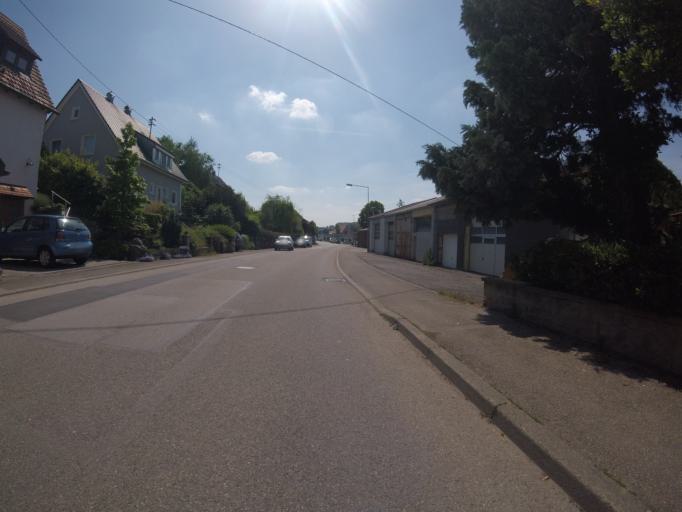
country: DE
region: Baden-Wuerttemberg
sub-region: Regierungsbezirk Stuttgart
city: Grossbottwar
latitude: 48.9998
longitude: 9.2982
